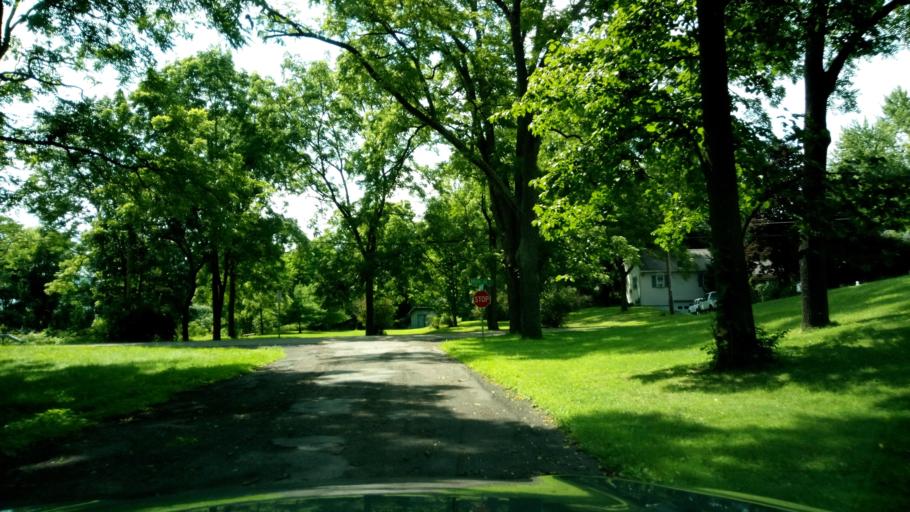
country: US
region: New York
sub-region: Chemung County
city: West Elmira
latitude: 42.0836
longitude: -76.8742
